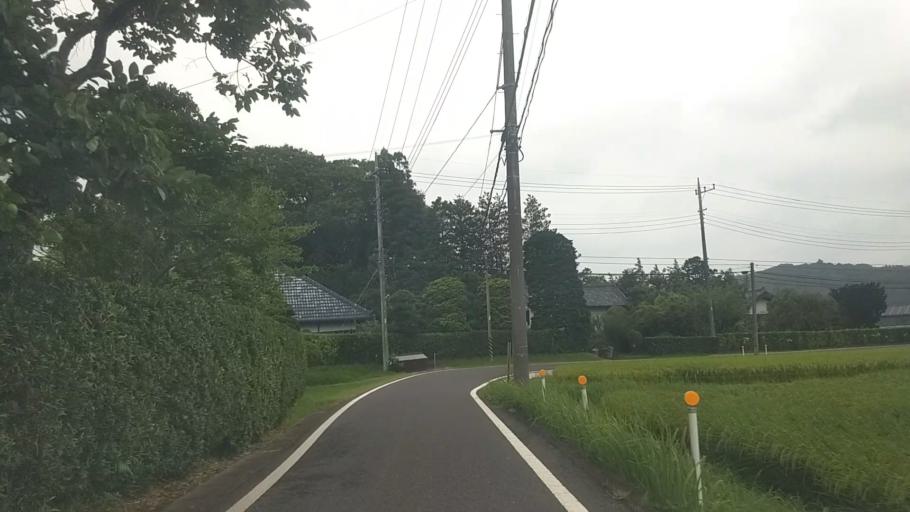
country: JP
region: Chiba
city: Kawaguchi
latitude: 35.2553
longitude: 140.0594
